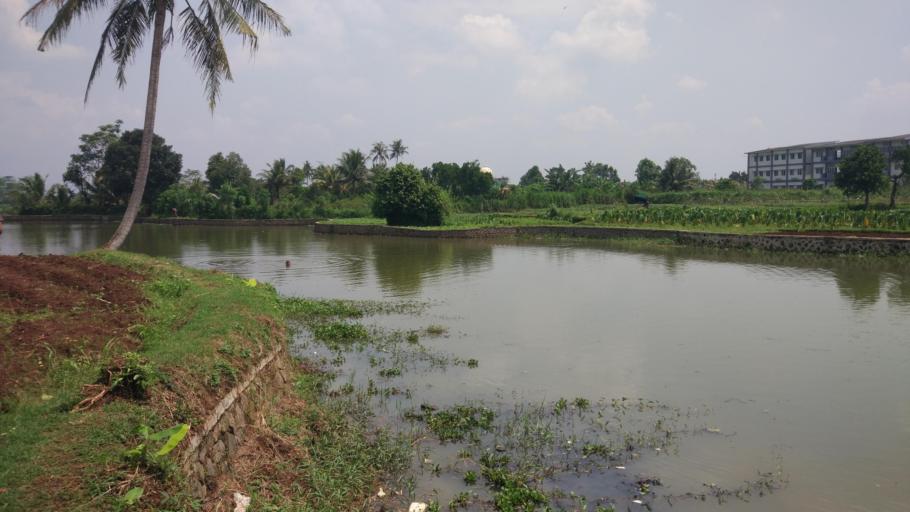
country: ID
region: West Java
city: Ciampea
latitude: -6.5478
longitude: 106.7405
